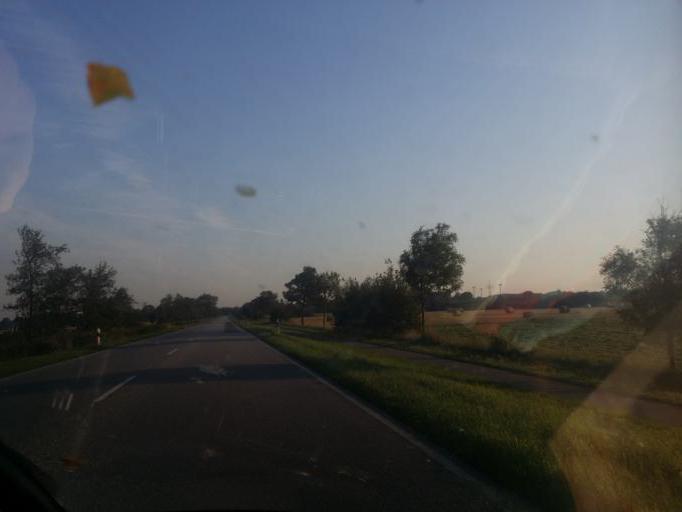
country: DE
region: Schleswig-Holstein
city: Struckum
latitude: 54.5742
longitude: 8.9999
